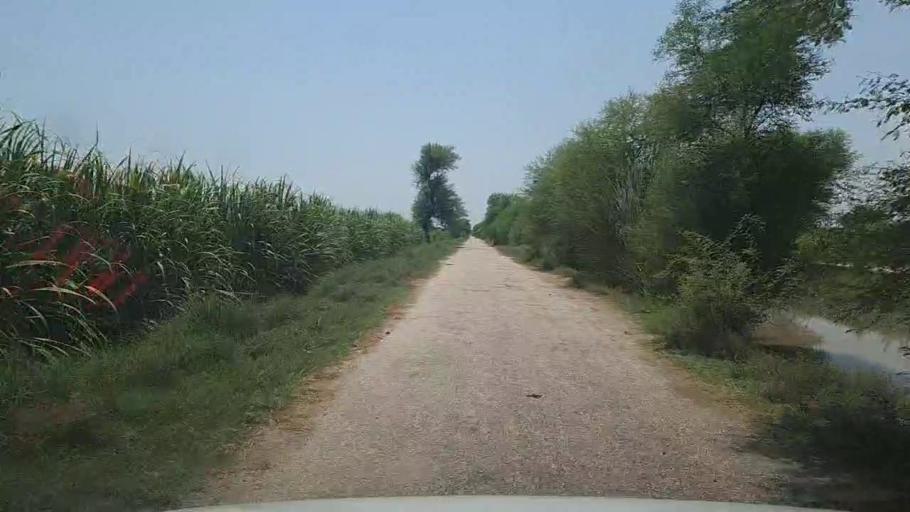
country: PK
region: Sindh
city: Ubauro
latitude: 28.1625
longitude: 69.7460
